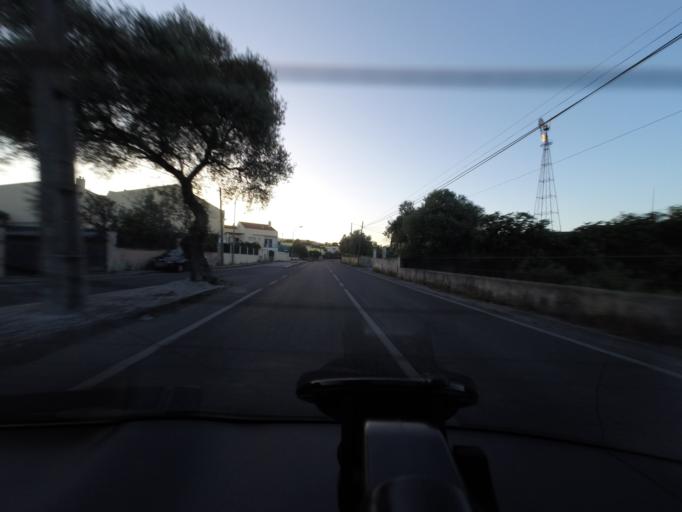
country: PT
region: Lisbon
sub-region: Sintra
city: Rio de Mouro
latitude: 38.7592
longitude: -9.3470
